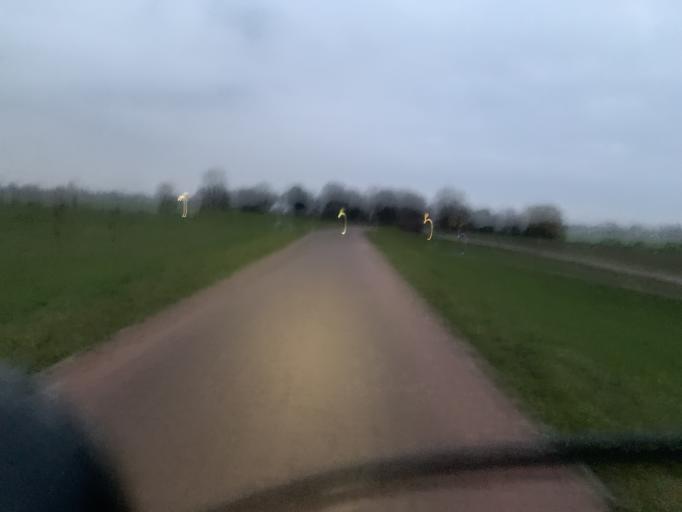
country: DE
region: North Rhine-Westphalia
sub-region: Regierungsbezirk Dusseldorf
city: Meerbusch
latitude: 51.3060
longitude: 6.7214
